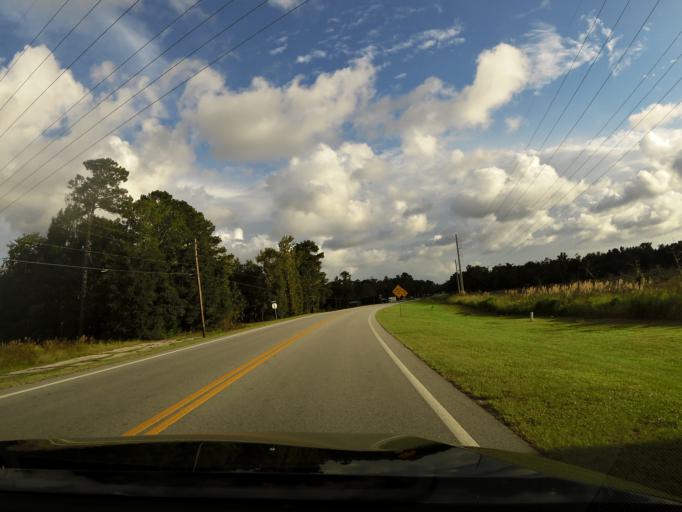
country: US
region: Georgia
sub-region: Liberty County
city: Midway
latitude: 31.7513
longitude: -81.4405
